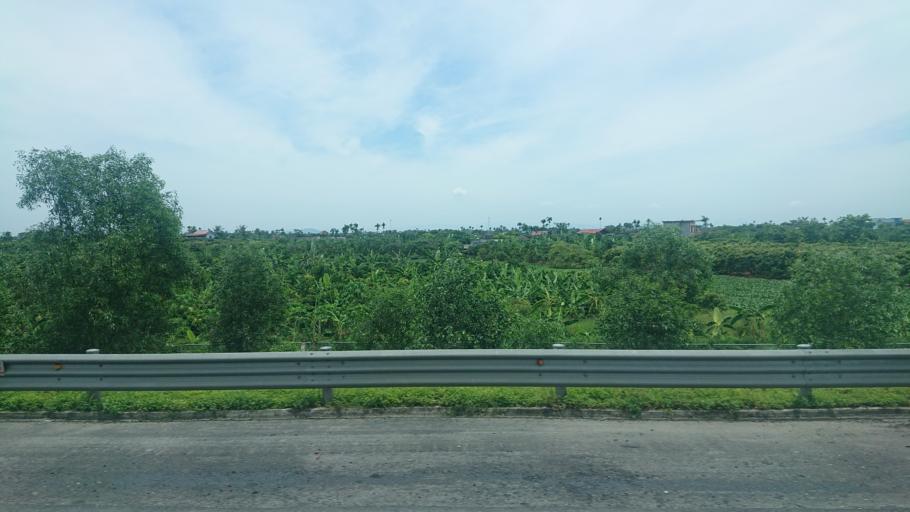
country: VN
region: Hai Duong
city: Tu Ky
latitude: 20.8217
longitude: 106.4746
